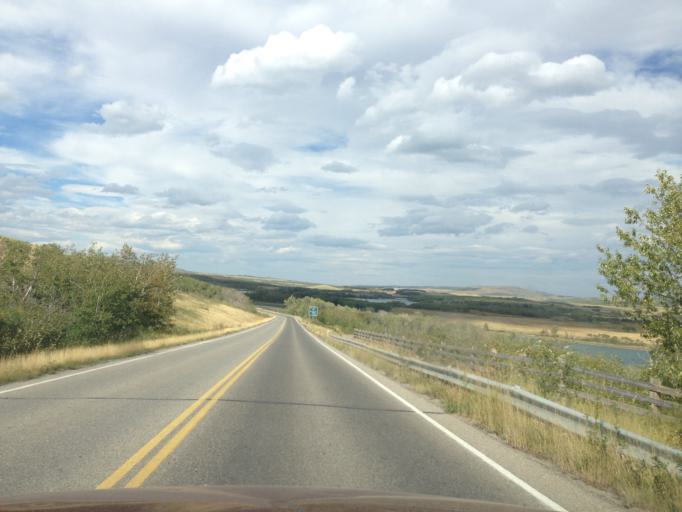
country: CA
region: Alberta
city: Pincher Creek
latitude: 49.1007
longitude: -113.8548
